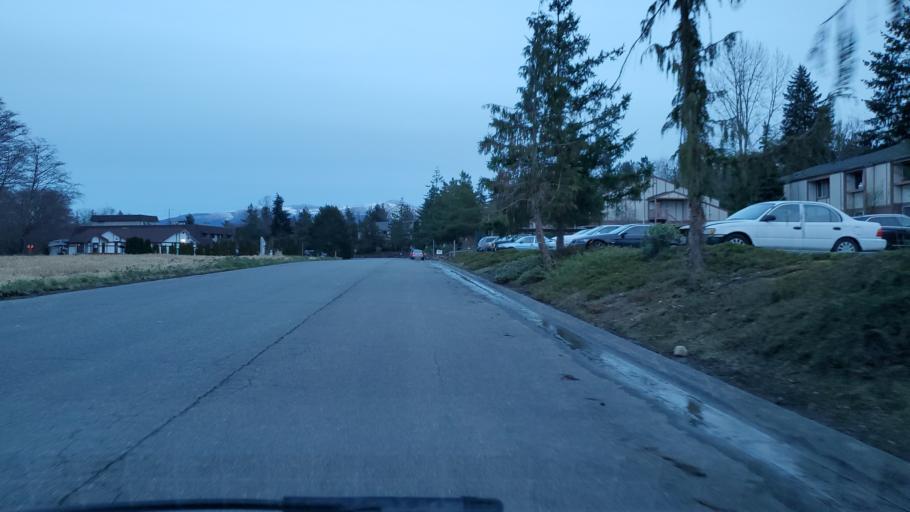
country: US
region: Washington
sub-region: Skagit County
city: Mount Vernon
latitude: 48.4328
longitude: -122.3233
